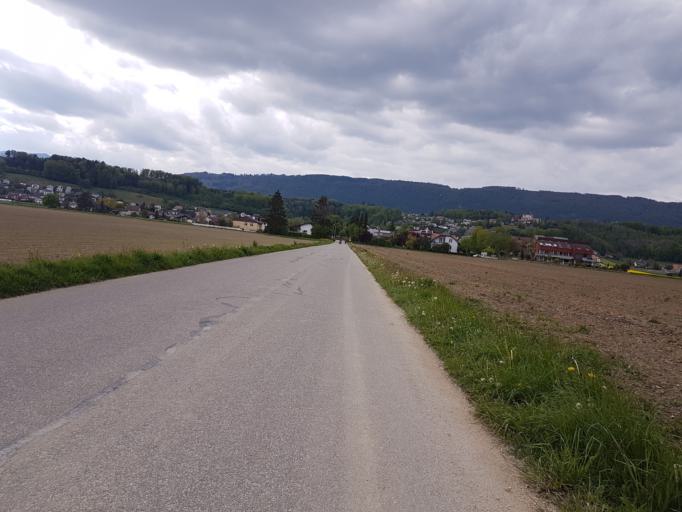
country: CH
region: Bern
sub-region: Biel/Bienne District
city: Meinisberg
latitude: 47.1443
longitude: 7.3307
